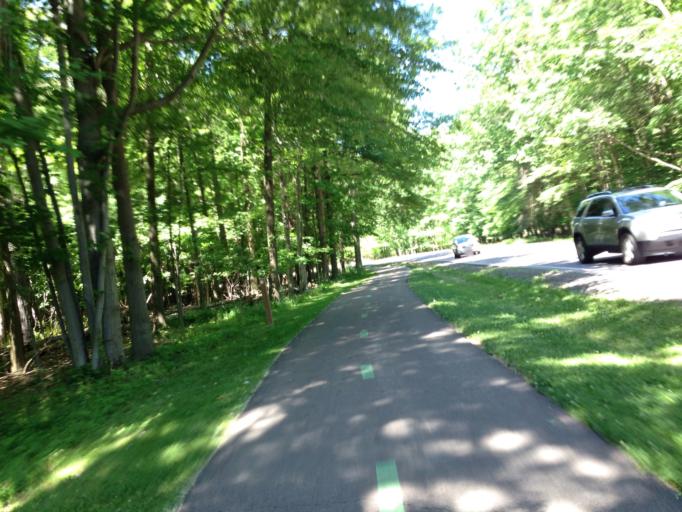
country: US
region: Ohio
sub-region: Cuyahoga County
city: Middleburg Heights
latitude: 41.3437
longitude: -81.8354
